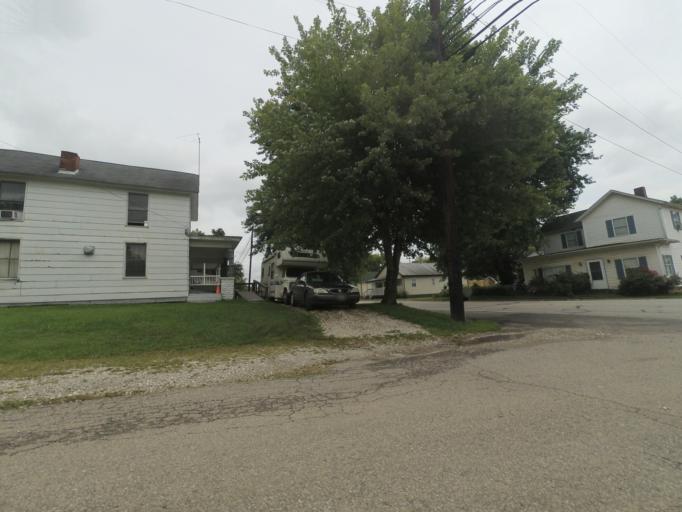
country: US
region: West Virginia
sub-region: Cabell County
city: Huntington
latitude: 38.4346
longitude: -82.4261
